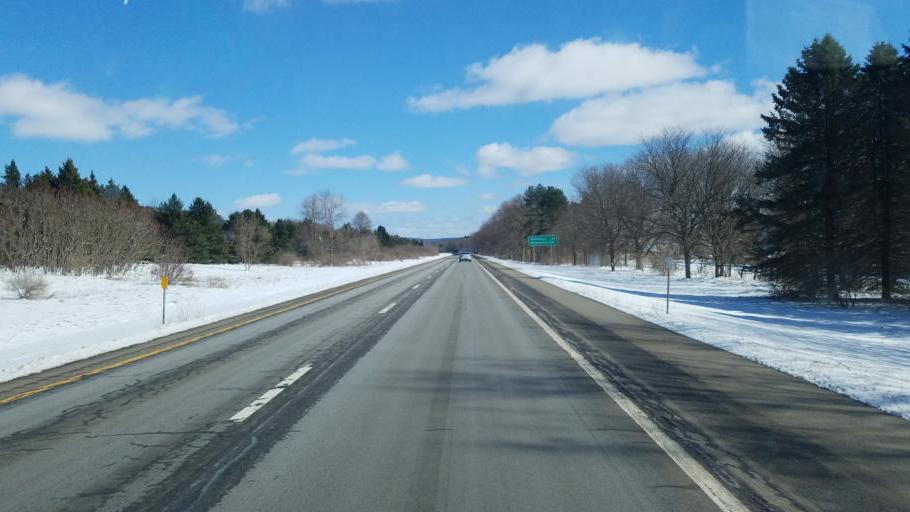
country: US
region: New York
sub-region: Chautauqua County
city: Falconer
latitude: 42.1362
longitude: -79.1556
